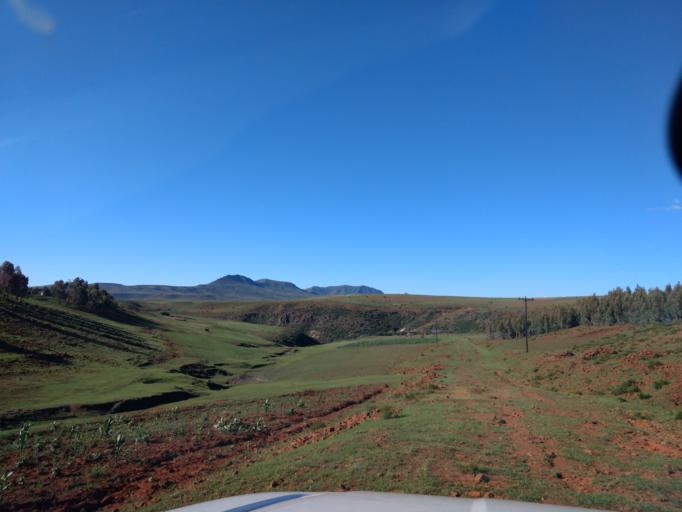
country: LS
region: Berea
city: Teyateyaneng
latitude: -29.3668
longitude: 27.7856
